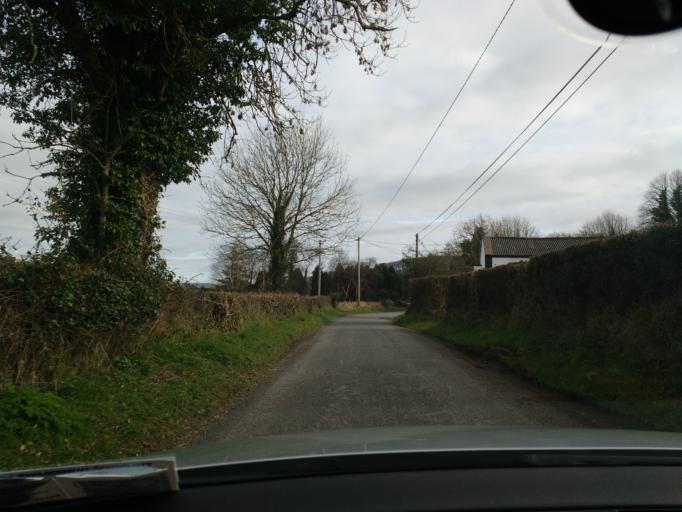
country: IE
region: Leinster
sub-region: Kilkenny
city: Callan
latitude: 52.6593
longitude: -7.5441
